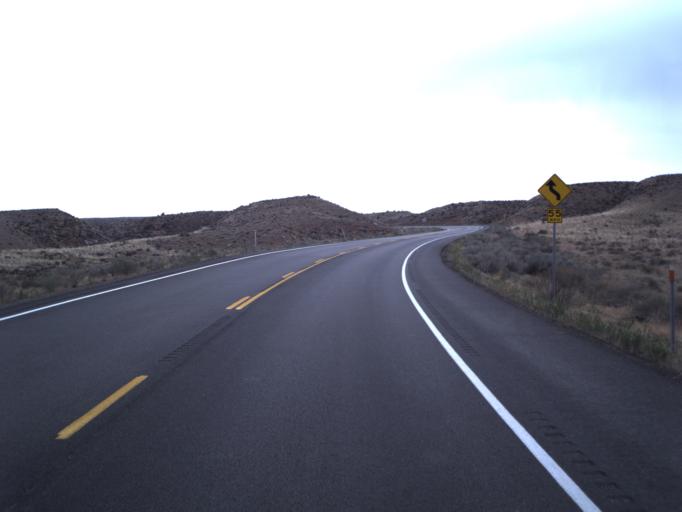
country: US
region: Utah
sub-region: Uintah County
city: Naples
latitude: 40.3067
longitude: -109.4803
